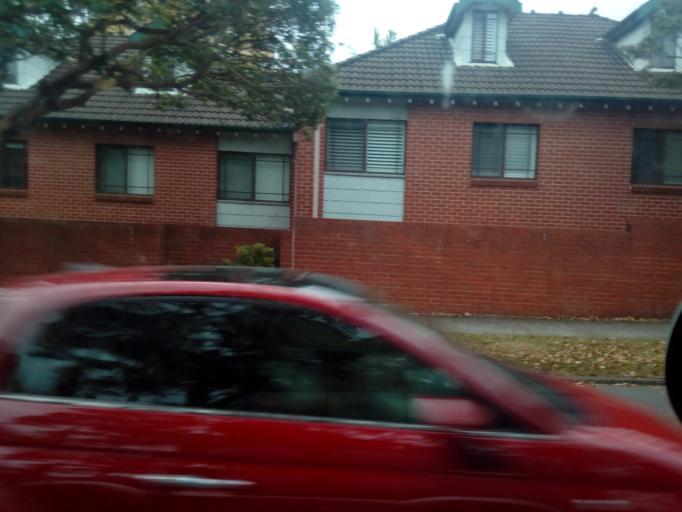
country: AU
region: New South Wales
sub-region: North Sydney
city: Cremorne
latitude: -33.8253
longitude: 151.2315
